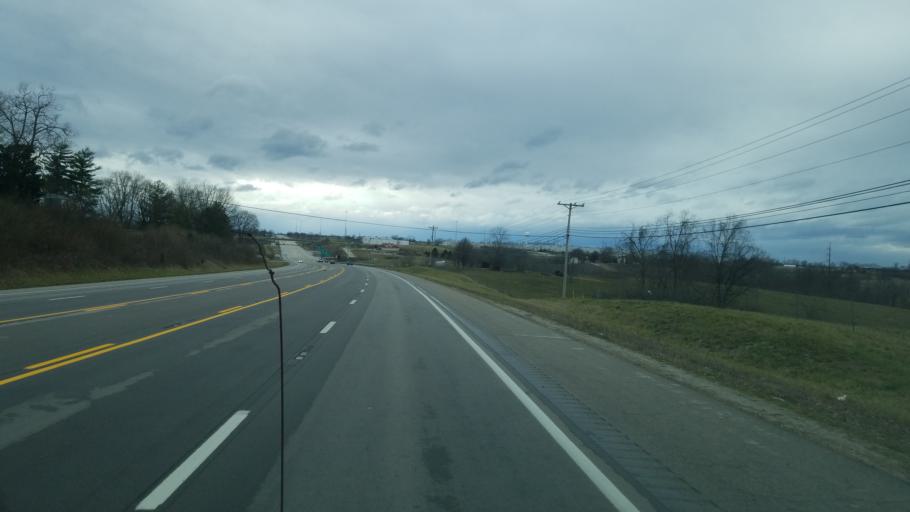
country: US
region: Ohio
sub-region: Brown County
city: Aberdeen
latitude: 38.6415
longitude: -83.8199
